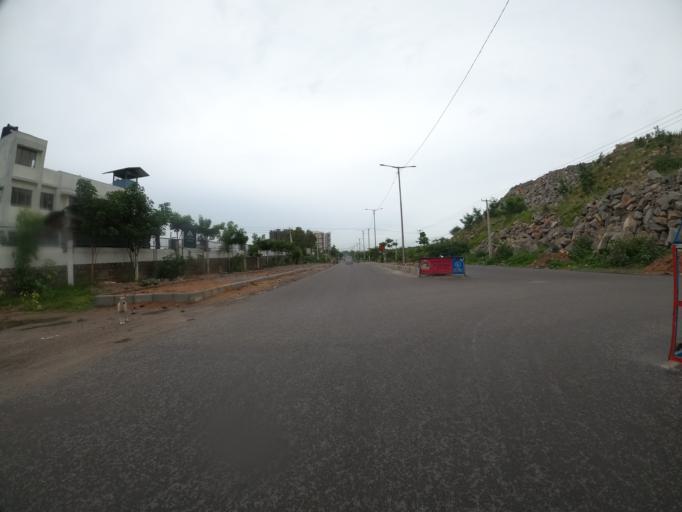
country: IN
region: Telangana
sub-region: Rangareddi
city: Kukatpalli
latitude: 17.4628
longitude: 78.3869
